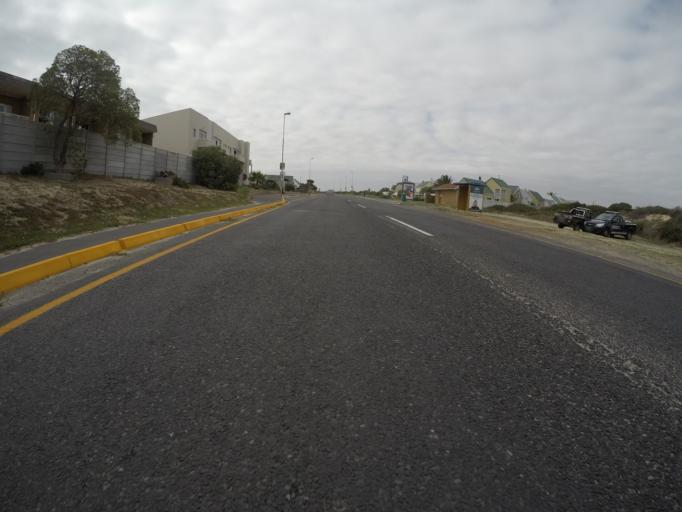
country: ZA
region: Western Cape
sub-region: City of Cape Town
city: Sunset Beach
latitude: -33.7118
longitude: 18.4461
